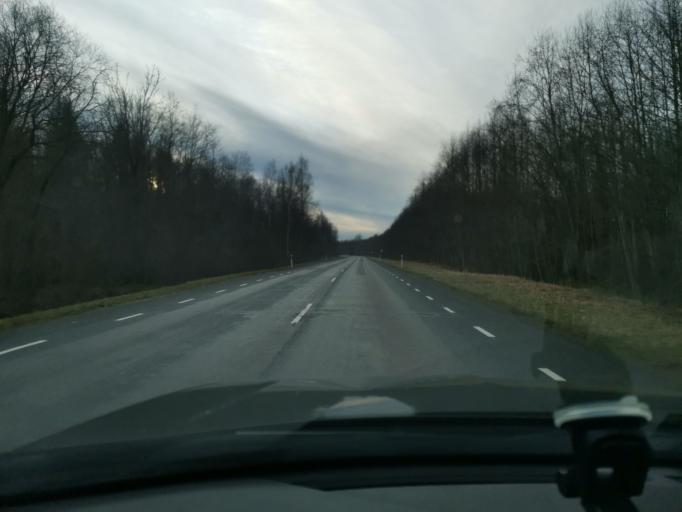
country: EE
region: Ida-Virumaa
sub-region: Sillamaee linn
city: Sillamae
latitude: 59.3253
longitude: 27.9245
